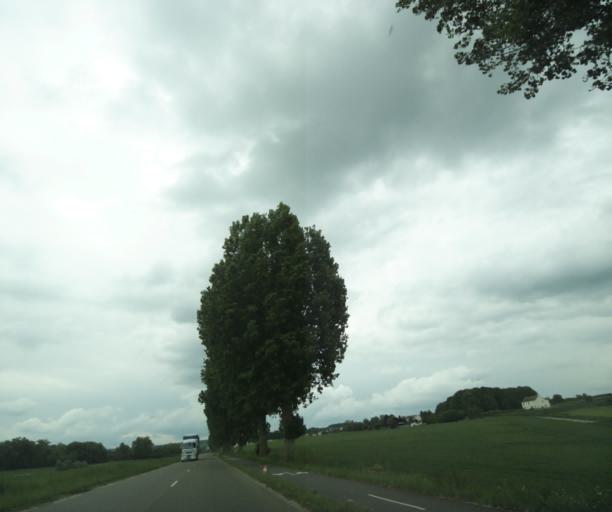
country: FR
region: Ile-de-France
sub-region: Departement des Yvelines
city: Ecquevilly
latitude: 48.9613
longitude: 1.9247
